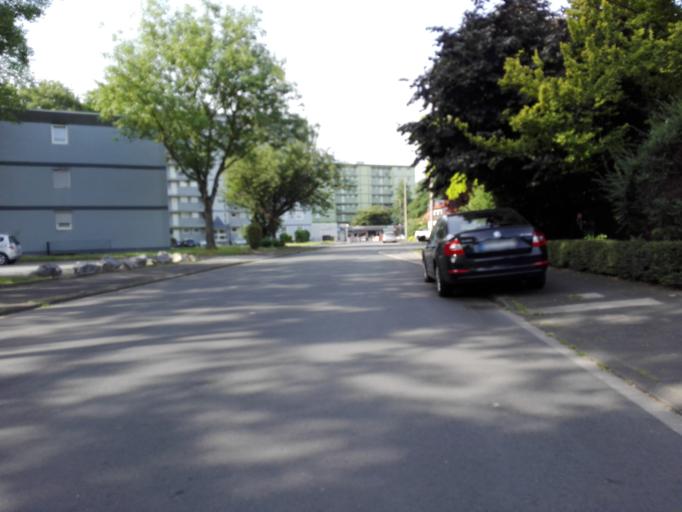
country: DE
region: North Rhine-Westphalia
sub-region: Regierungsbezirk Arnsberg
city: Unna
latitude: 51.5256
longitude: 7.6798
